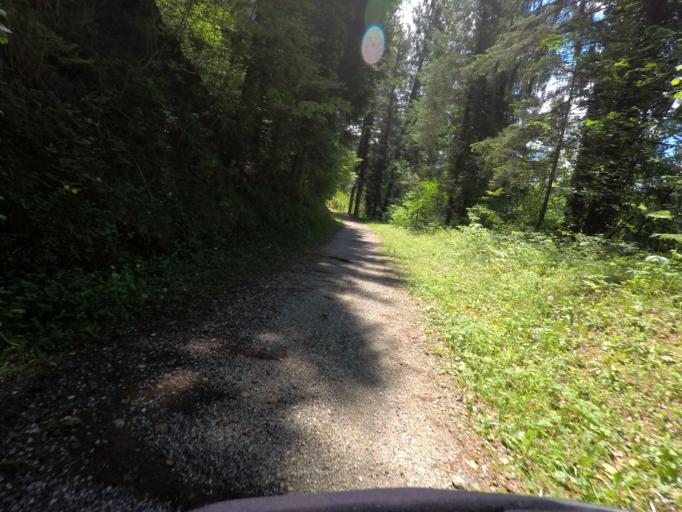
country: IT
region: Friuli Venezia Giulia
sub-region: Provincia di Udine
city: Ovaro
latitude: 46.4741
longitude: 12.8728
